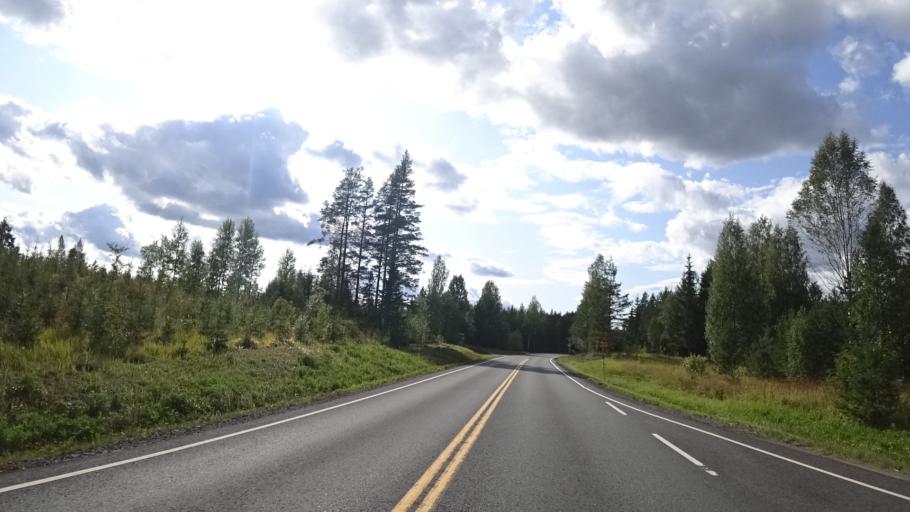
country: FI
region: North Karelia
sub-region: Keski-Karjala
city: Tohmajaervi
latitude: 62.1847
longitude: 30.5072
